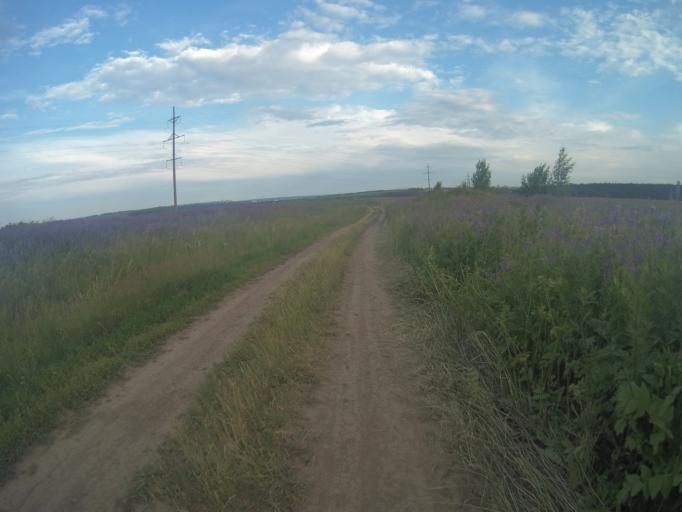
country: RU
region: Vladimir
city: Vladimir
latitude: 56.2098
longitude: 40.3750
